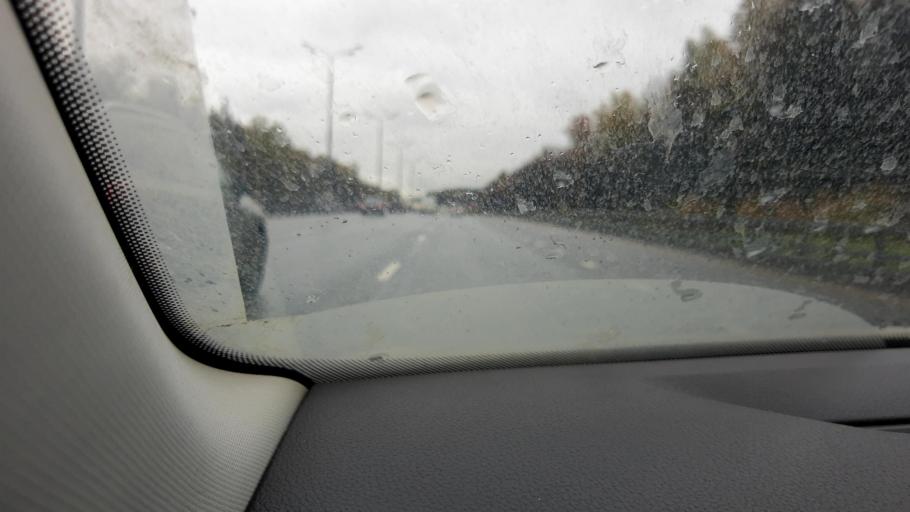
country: RU
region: Moskovskaya
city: Aprelevka
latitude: 55.5471
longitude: 37.1157
